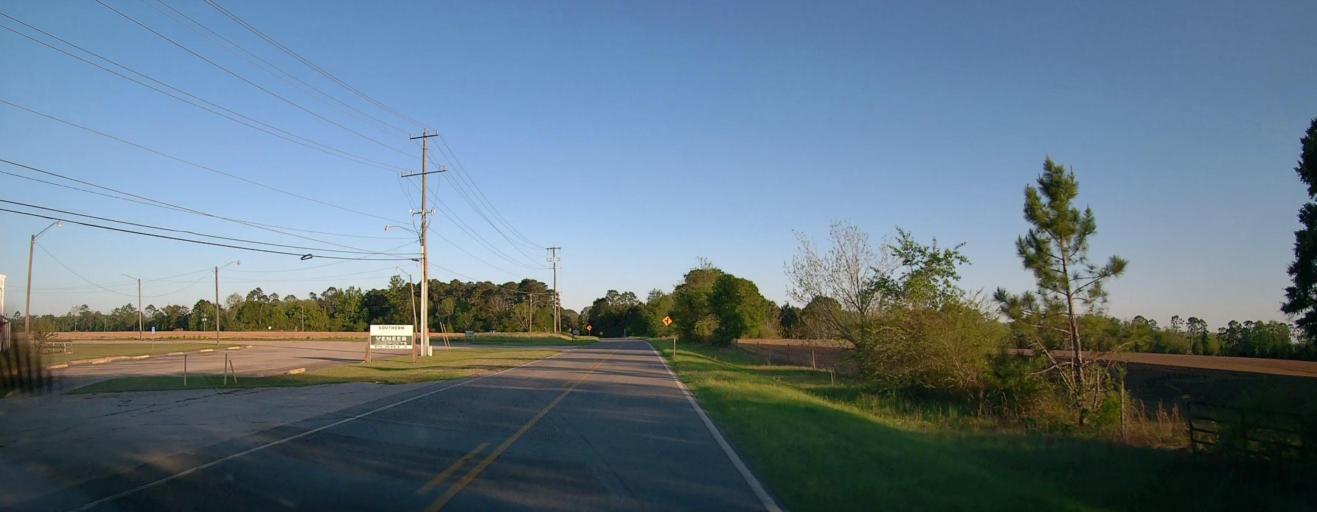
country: US
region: Georgia
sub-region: Ben Hill County
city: Fitzgerald
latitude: 31.6937
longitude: -83.2354
